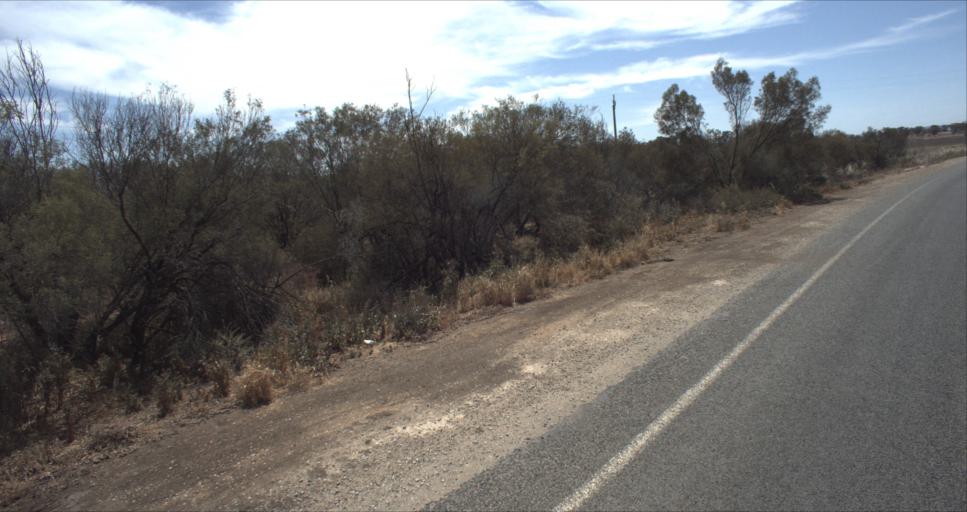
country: AU
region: New South Wales
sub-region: Leeton
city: Leeton
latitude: -34.6631
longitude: 146.4490
